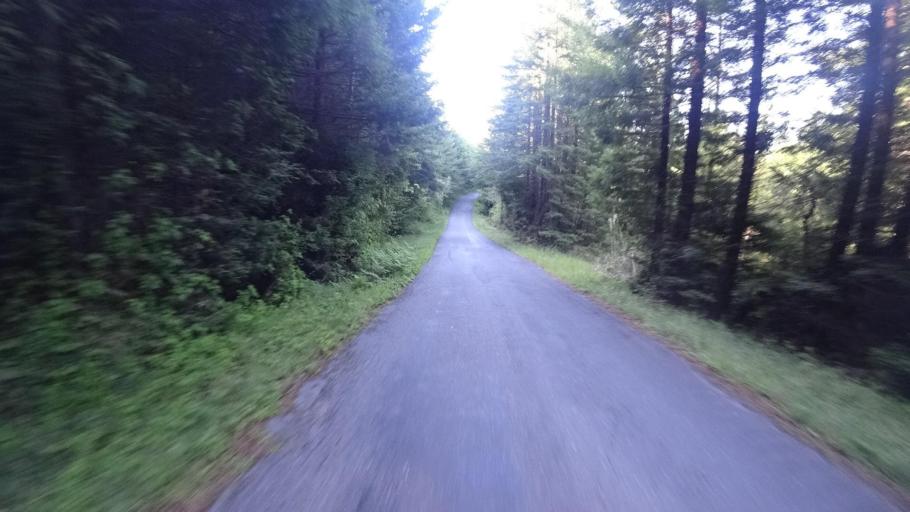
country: US
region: California
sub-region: Humboldt County
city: Rio Dell
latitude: 40.4476
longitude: -123.9770
